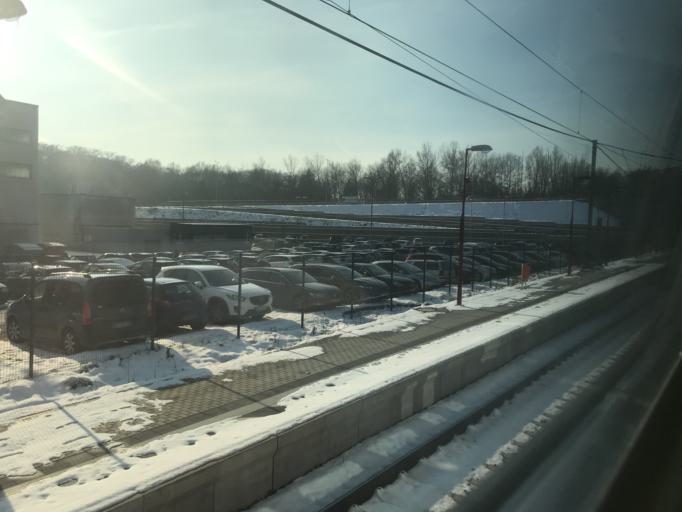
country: LU
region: Luxembourg
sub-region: Canton de Luxembourg
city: Sandweiler
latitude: 49.5991
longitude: 6.2140
